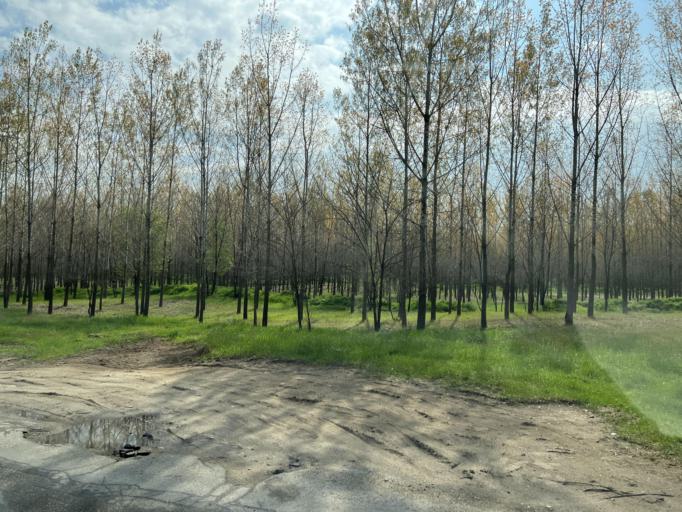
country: HU
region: Pest
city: Hernad
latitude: 47.1751
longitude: 19.4734
